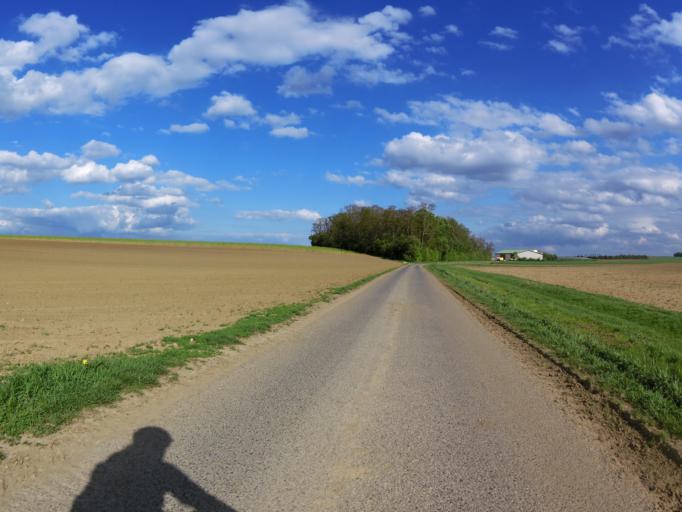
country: DE
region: Bavaria
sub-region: Regierungsbezirk Unterfranken
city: Unterpleichfeld
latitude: 49.8645
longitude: 10.0553
